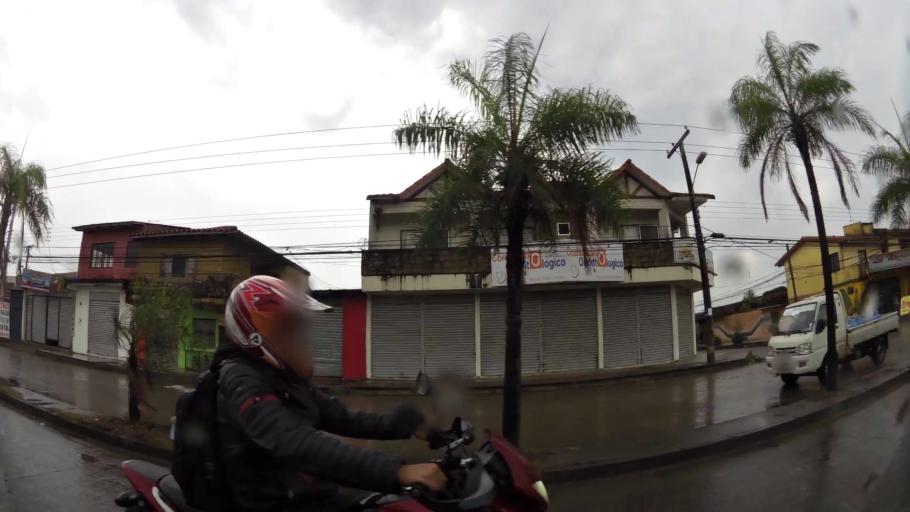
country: BO
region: Santa Cruz
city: Santa Cruz de la Sierra
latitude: -17.7586
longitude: -63.1564
